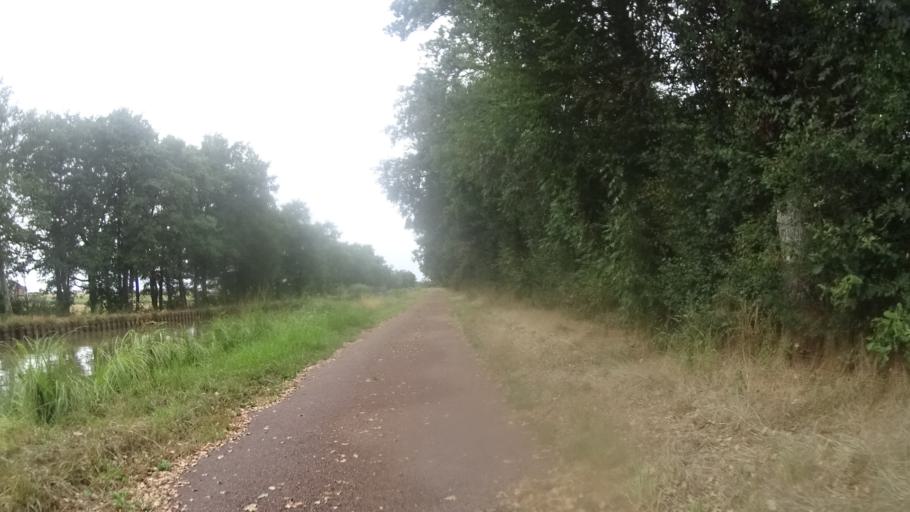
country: FR
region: Bourgogne
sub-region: Departement de la Nievre
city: Imphy
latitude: 46.8528
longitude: 3.2973
